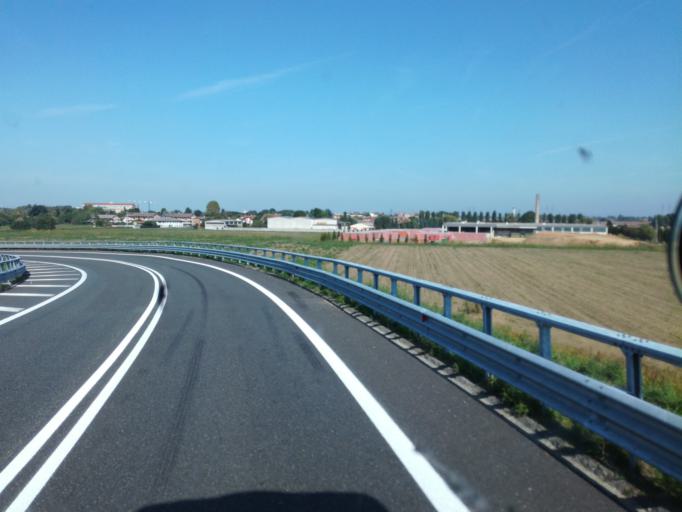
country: IT
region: Lombardy
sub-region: Citta metropolitana di Milano
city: Vizzolo Predabissi
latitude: 45.3511
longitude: 9.3521
